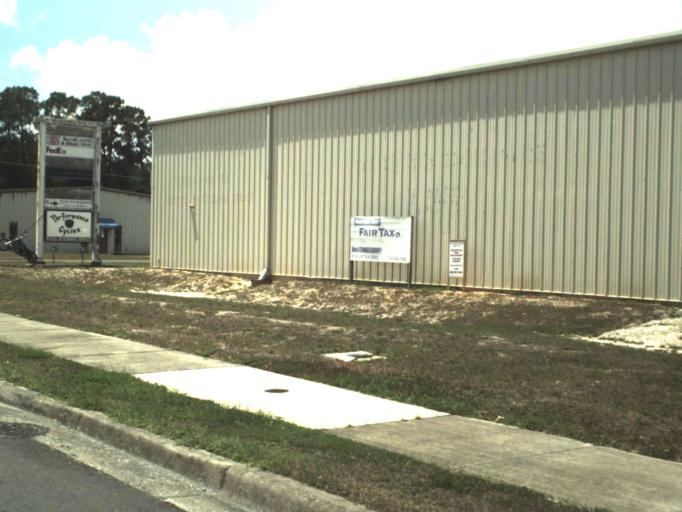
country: US
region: Florida
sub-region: Lake County
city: Leesburg
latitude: 28.8114
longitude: -81.9234
